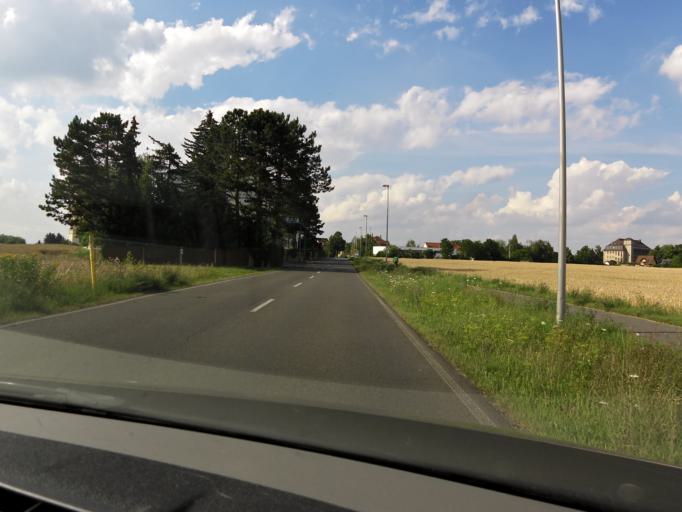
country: DE
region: Saxony
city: Taucha
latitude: 51.3298
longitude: 12.4812
